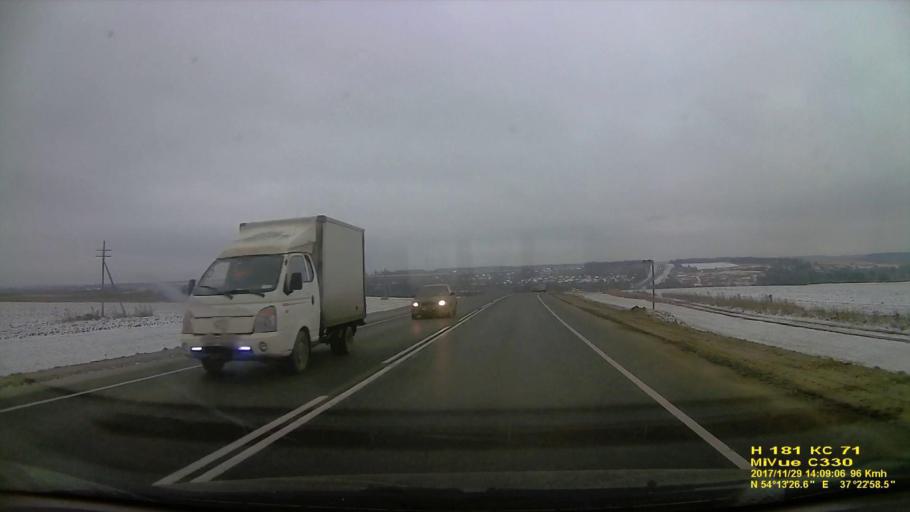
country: RU
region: Tula
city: Leninskiy
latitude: 54.2238
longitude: 37.3835
